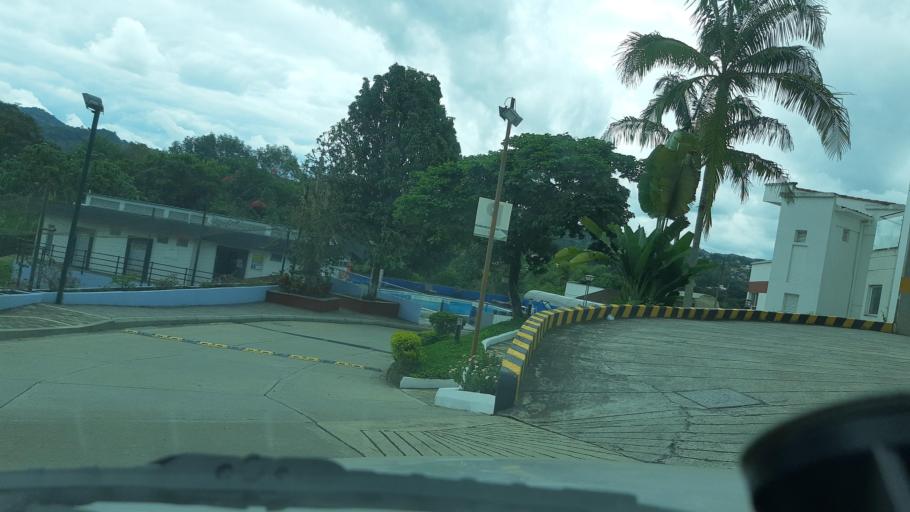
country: CO
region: Boyaca
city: Moniquira
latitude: 5.8816
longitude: -73.5782
